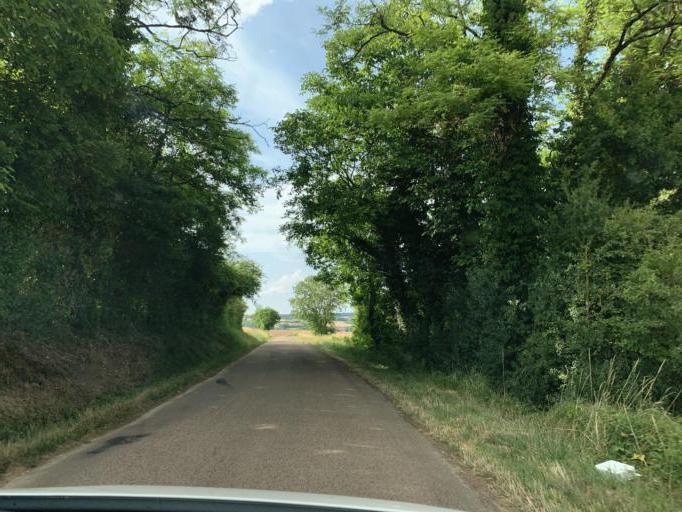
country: FR
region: Bourgogne
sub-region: Departement de l'Yonne
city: Fontenailles
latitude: 47.4697
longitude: 3.4275
